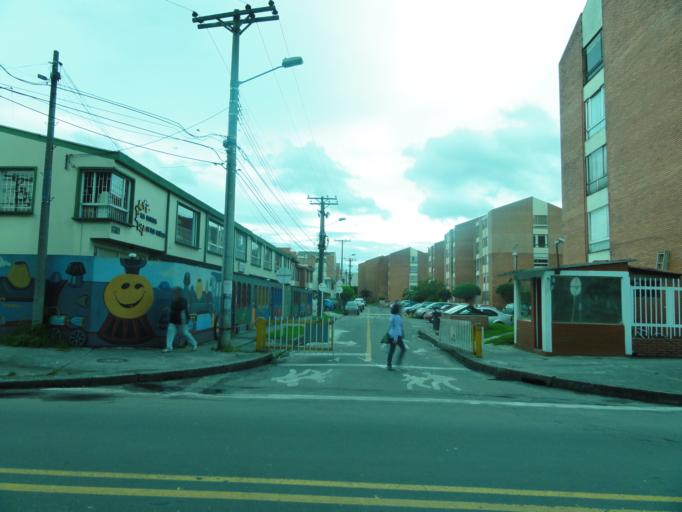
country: CO
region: Bogota D.C.
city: Bogota
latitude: 4.6516
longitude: -74.0852
